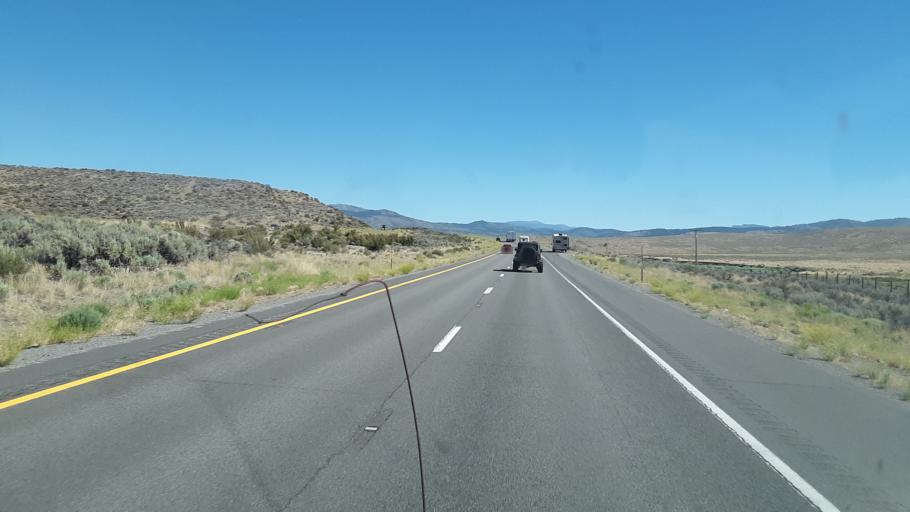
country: US
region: Nevada
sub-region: Washoe County
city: Cold Springs
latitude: 39.7062
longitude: -120.0346
